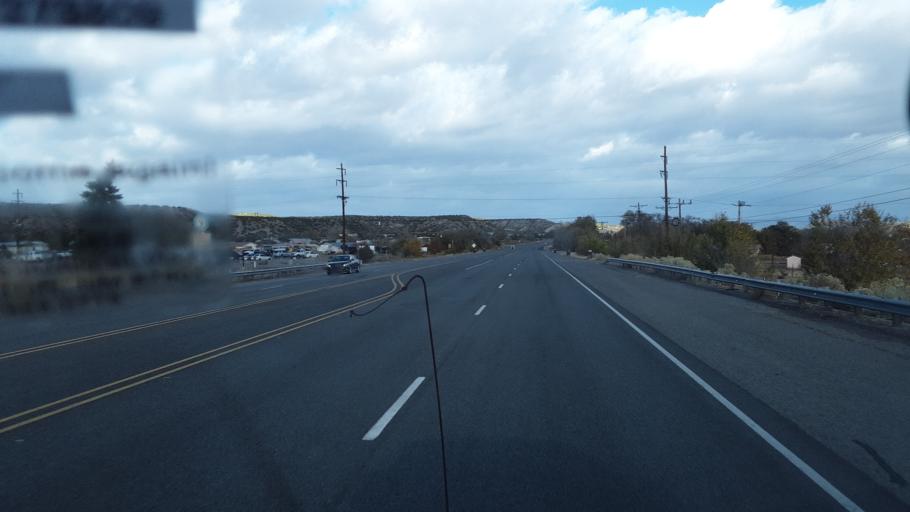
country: US
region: New Mexico
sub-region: Rio Arriba County
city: Ohkay Owingeh
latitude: 36.0461
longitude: -106.1076
